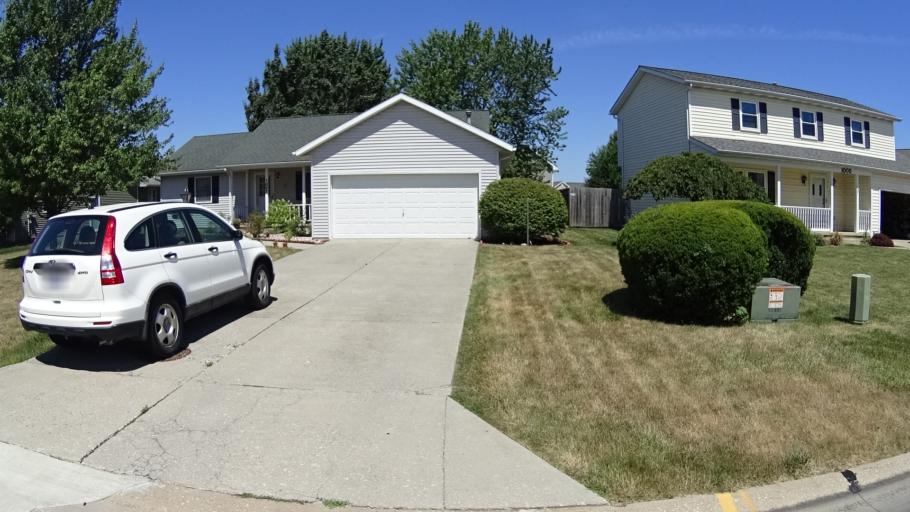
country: US
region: Ohio
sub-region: Erie County
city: Sandusky
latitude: 41.4015
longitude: -82.6937
